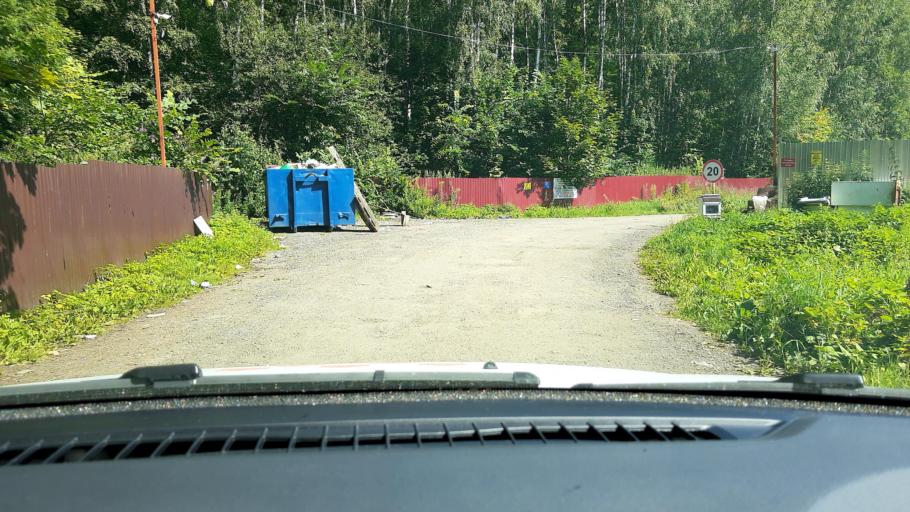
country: RU
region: Nizjnij Novgorod
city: Kstovo
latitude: 56.0542
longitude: 43.9952
